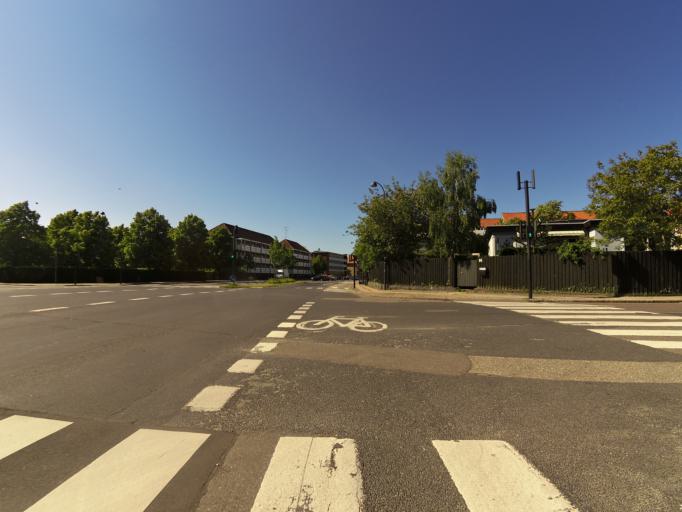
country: DK
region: Capital Region
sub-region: Lyngby-Tarbaek Kommune
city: Kongens Lyngby
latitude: 55.7496
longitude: 12.5206
